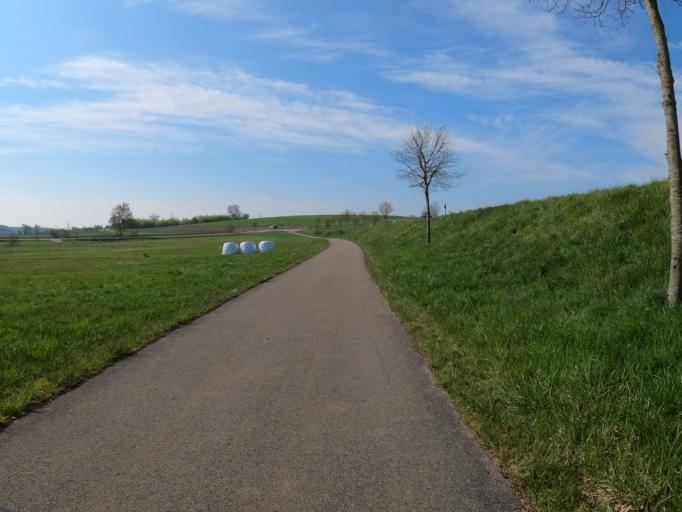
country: DE
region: Bavaria
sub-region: Swabia
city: Pfaffenhofen an der Roth
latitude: 48.3905
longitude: 10.1895
